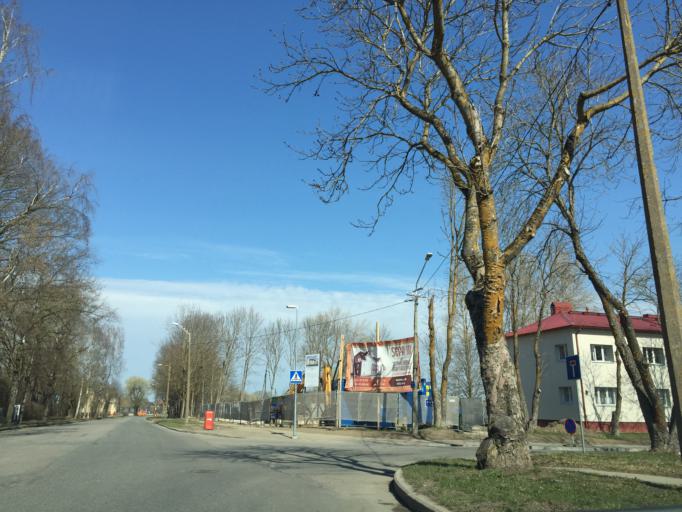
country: EE
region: Ida-Virumaa
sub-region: Narva linn
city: Narva
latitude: 59.3838
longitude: 28.2002
